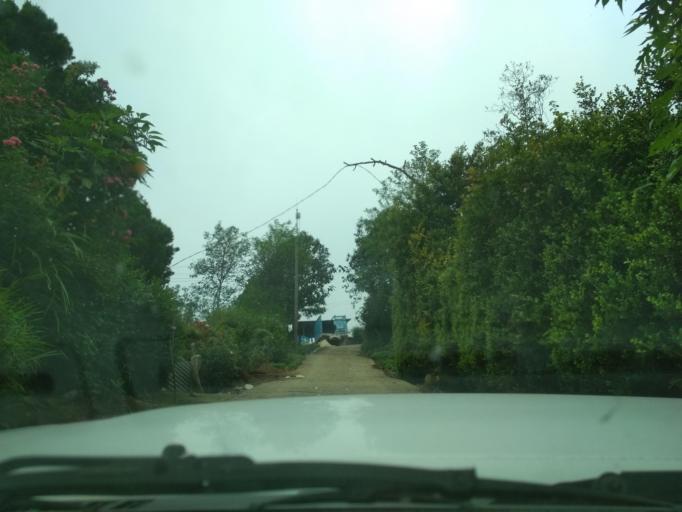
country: MX
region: Veracruz
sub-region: La Perla
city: Chilapa
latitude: 18.9667
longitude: -97.1696
